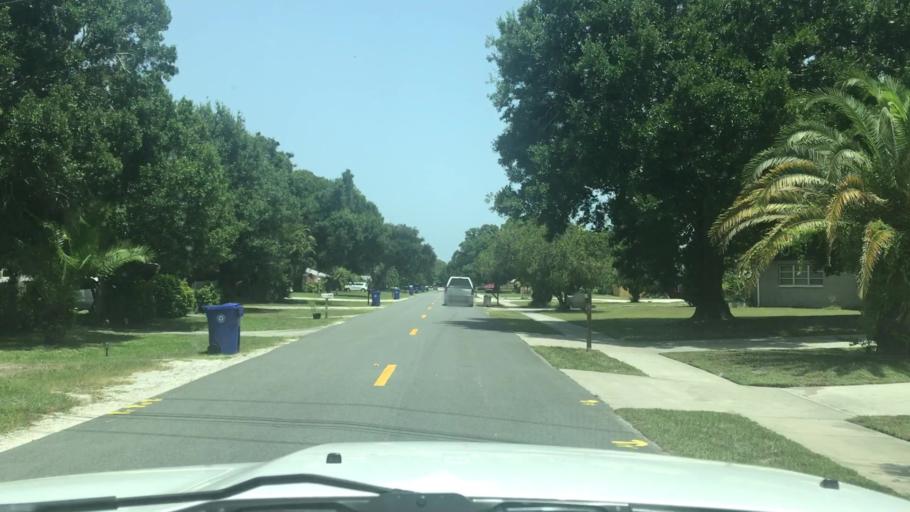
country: US
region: Florida
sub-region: Indian River County
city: Vero Beach
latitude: 27.6427
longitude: -80.4174
